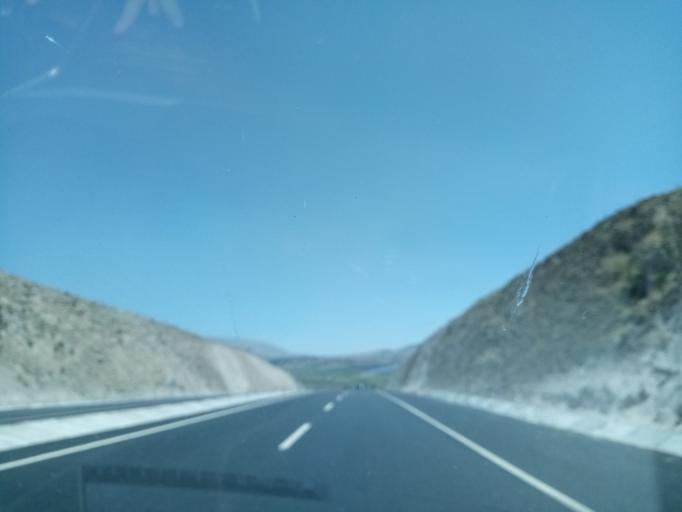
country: TR
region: Konya
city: Kiziloren
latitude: 37.7562
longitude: 32.2088
